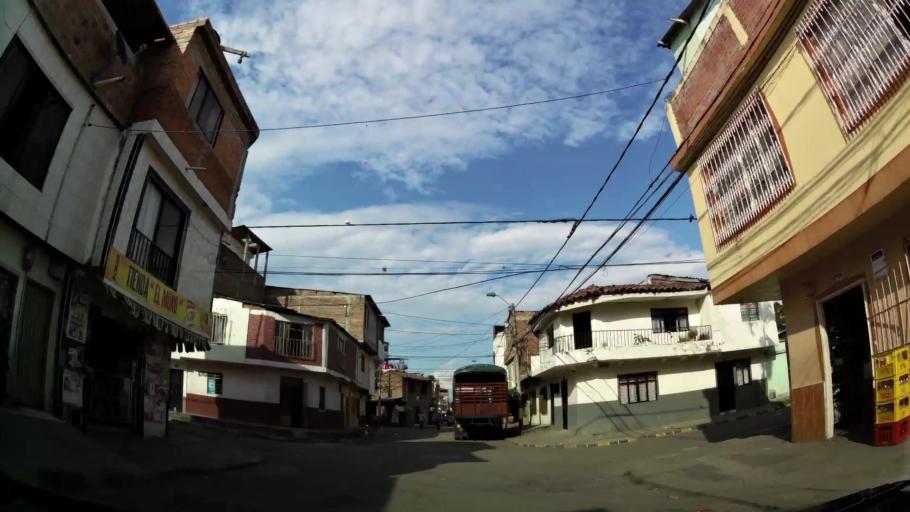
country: CO
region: Valle del Cauca
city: Cali
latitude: 3.4712
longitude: -76.5144
